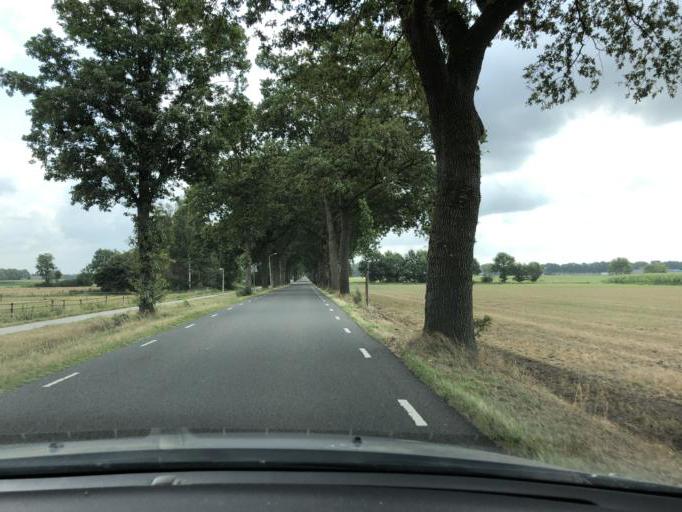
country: NL
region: Drenthe
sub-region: Gemeente Hoogeveen
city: Hoogeveen
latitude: 52.6732
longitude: 6.4614
